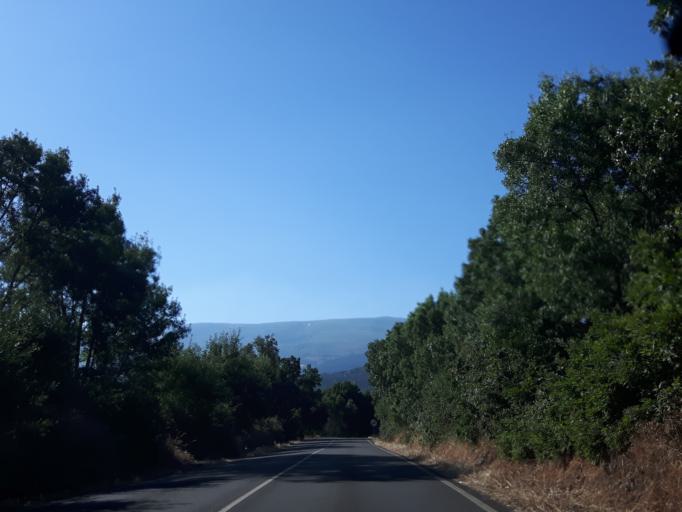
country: ES
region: Castille and Leon
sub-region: Provincia de Salamanca
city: Navalmoral de Bejar
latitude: 40.4013
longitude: -5.7868
